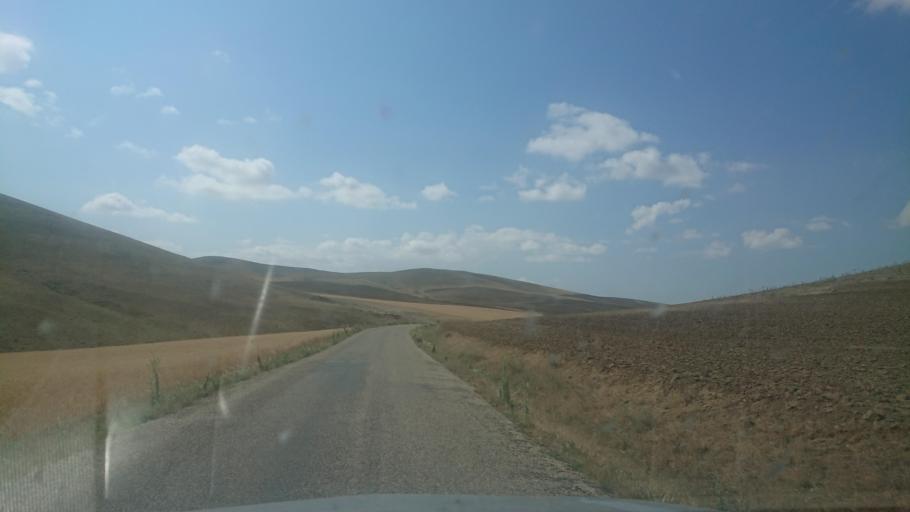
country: TR
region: Aksaray
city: Sariyahsi
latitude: 39.0100
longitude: 33.9488
